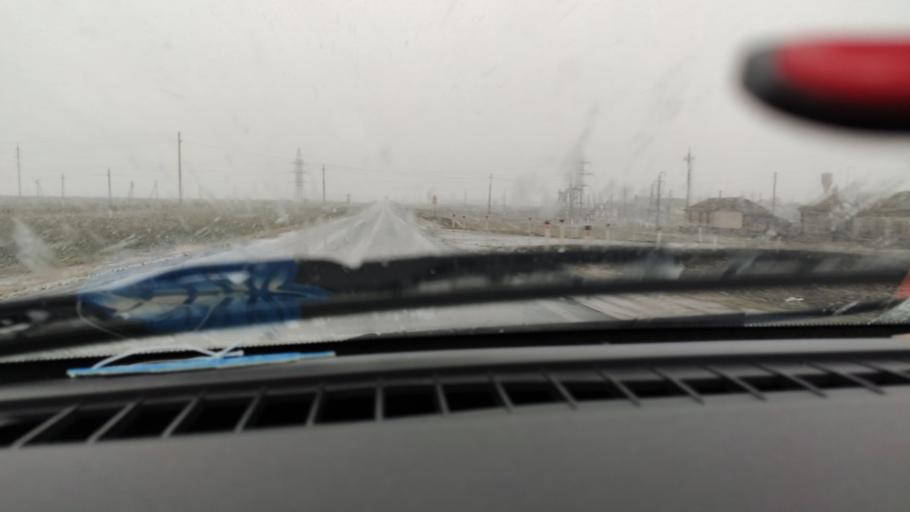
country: RU
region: Tatarstan
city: Cheremshan
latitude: 54.7218
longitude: 51.2621
